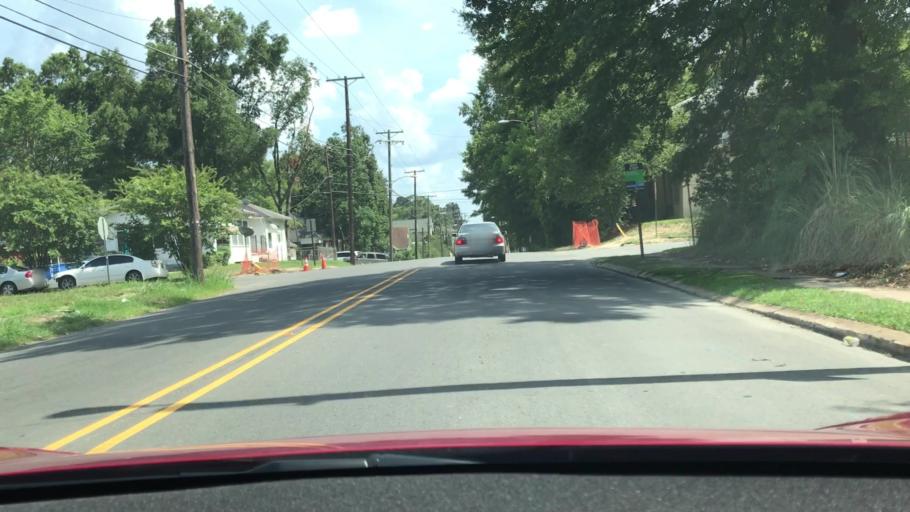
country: US
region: Louisiana
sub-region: Bossier Parish
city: Bossier City
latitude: 32.4993
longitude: -93.7332
